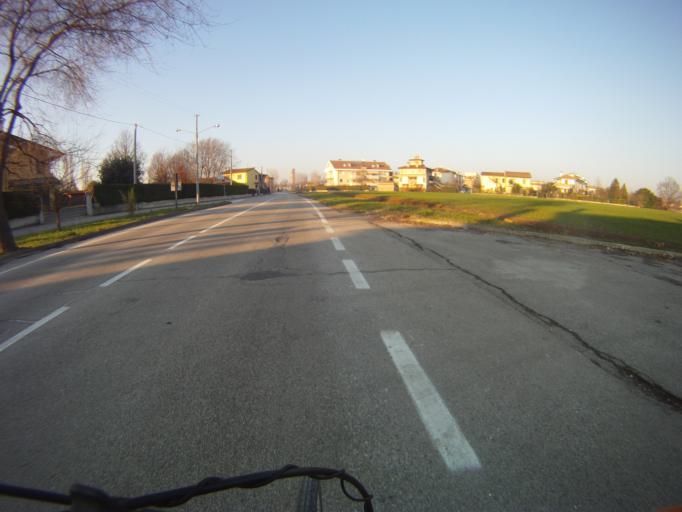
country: IT
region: Veneto
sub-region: Provincia di Padova
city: Ponte San Nicolo
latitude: 45.3733
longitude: 11.9049
